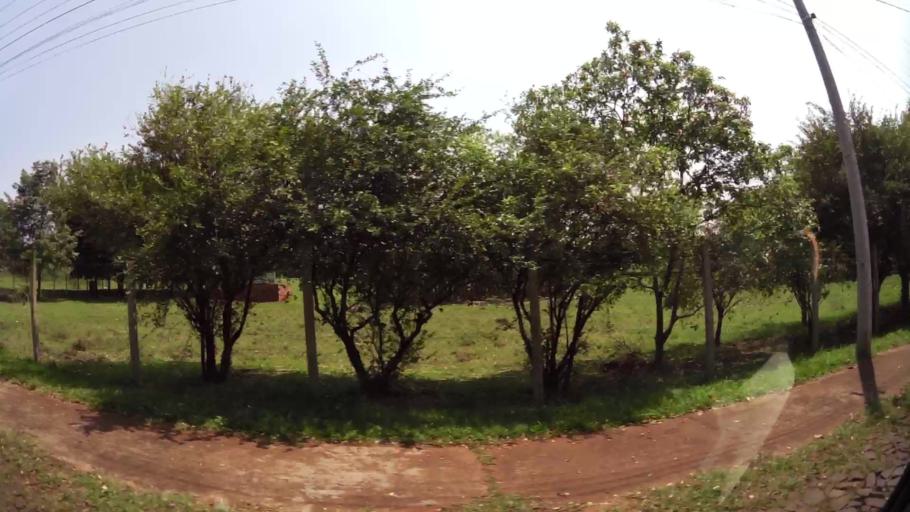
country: PY
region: Alto Parana
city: Presidente Franco
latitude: -25.5248
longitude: -54.6084
